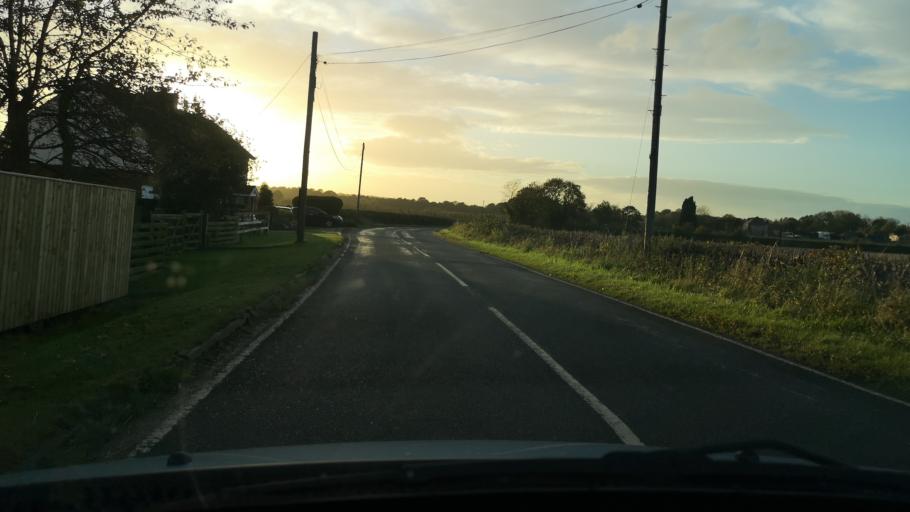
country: GB
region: England
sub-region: City and Borough of Wakefield
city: Badsworth
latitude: 53.6489
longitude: -1.3013
